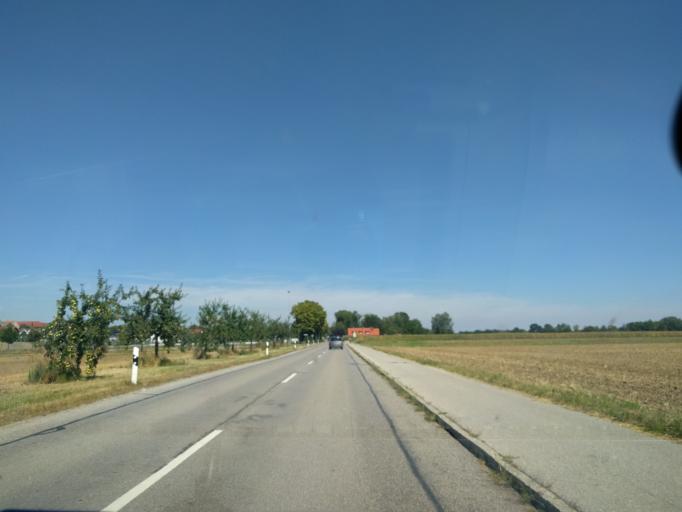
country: DE
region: Bavaria
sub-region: Upper Bavaria
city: Fuerstenfeldbruck
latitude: 48.1835
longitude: 11.2250
